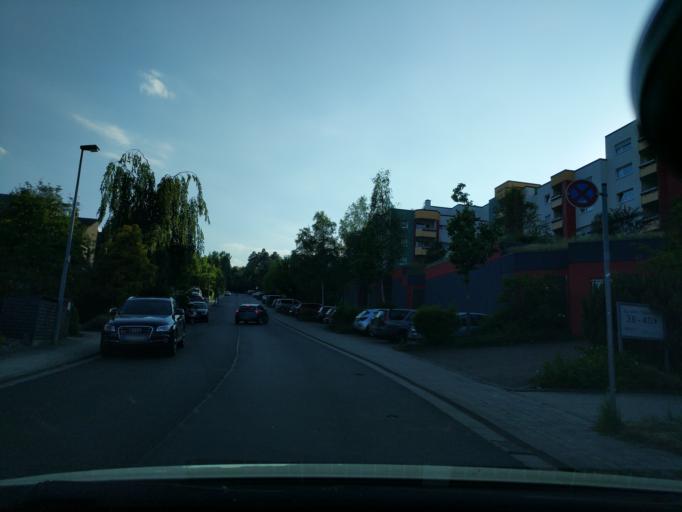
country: DE
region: Rheinland-Pfalz
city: Kaiserslautern
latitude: 49.4251
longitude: 7.7438
